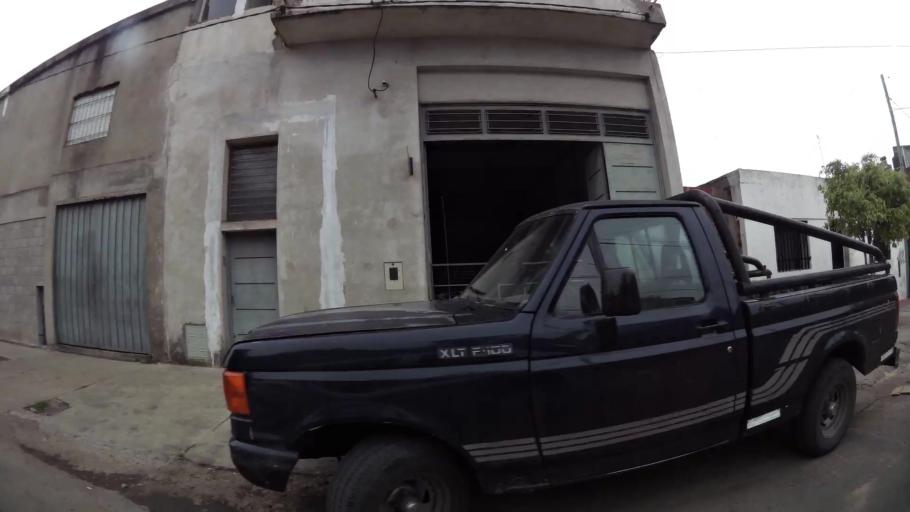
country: AR
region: Santa Fe
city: Gobernador Galvez
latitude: -33.0007
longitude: -60.6620
